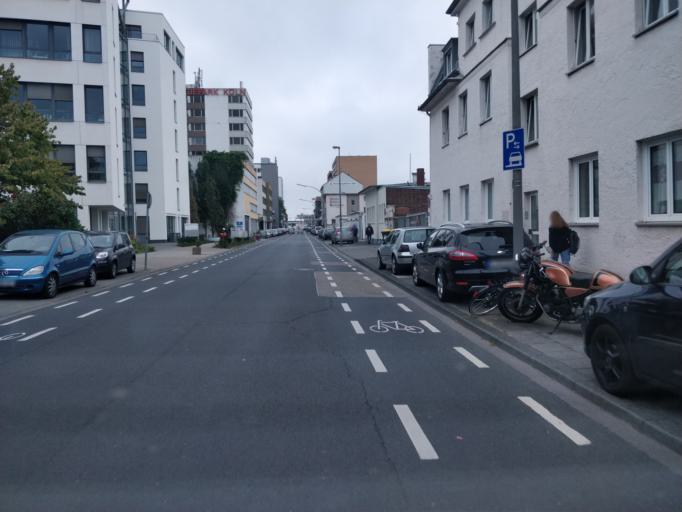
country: DE
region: North Rhine-Westphalia
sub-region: Regierungsbezirk Koln
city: Mengenich
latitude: 50.9434
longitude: 6.8896
